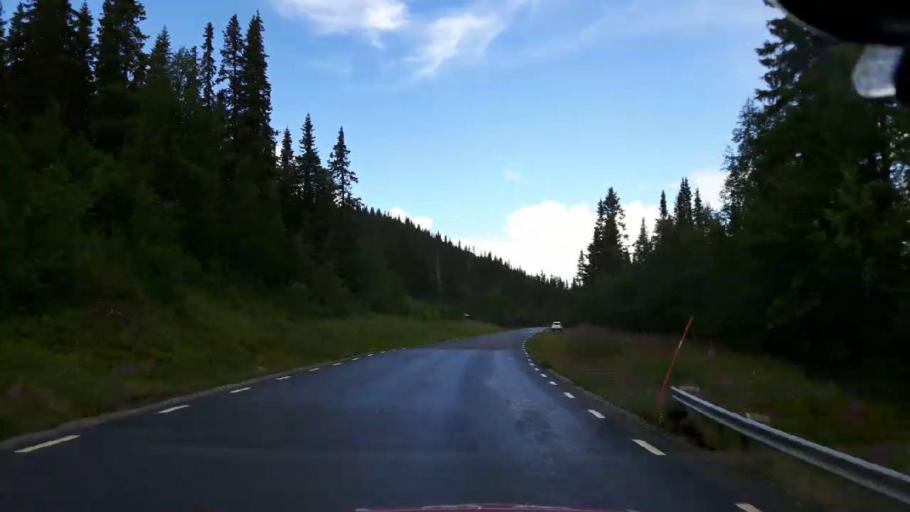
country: SE
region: Vaesterbotten
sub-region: Vilhelmina Kommun
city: Sjoberg
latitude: 64.9969
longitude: 15.2050
